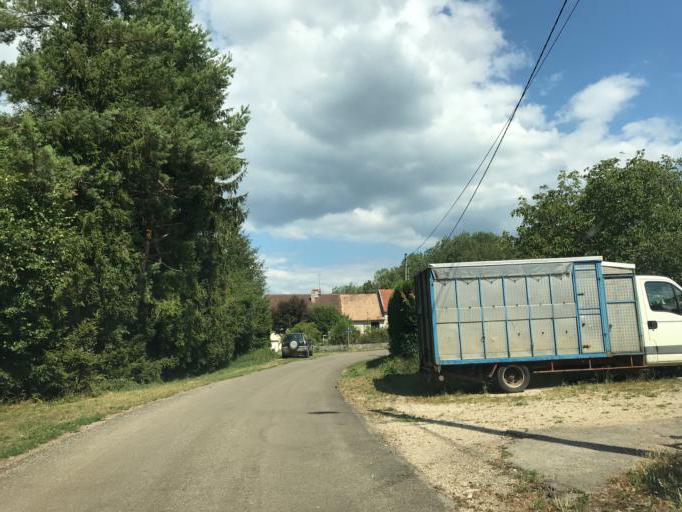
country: FR
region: Franche-Comte
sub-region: Departement du Jura
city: Clairvaux-les-Lacs
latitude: 46.5924
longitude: 5.7365
